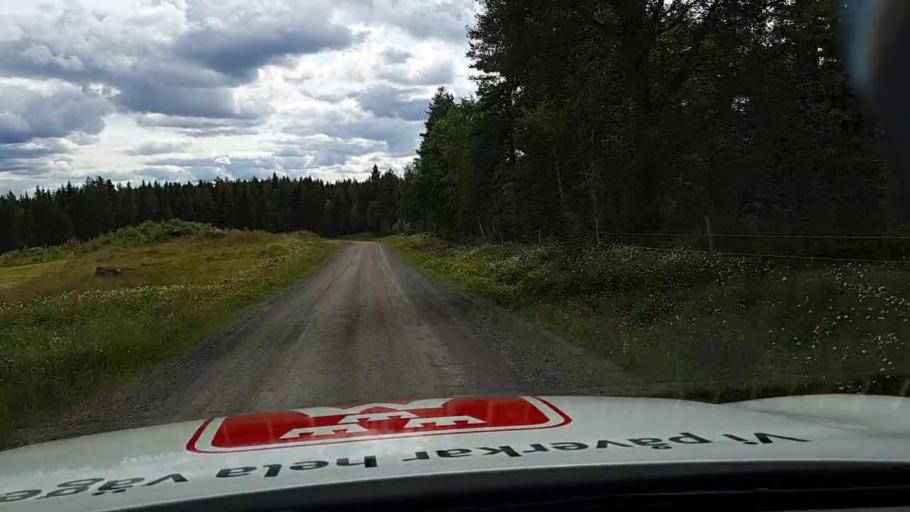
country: SE
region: Jaemtland
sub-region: Braecke Kommun
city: Braecke
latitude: 63.2803
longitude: 15.3711
